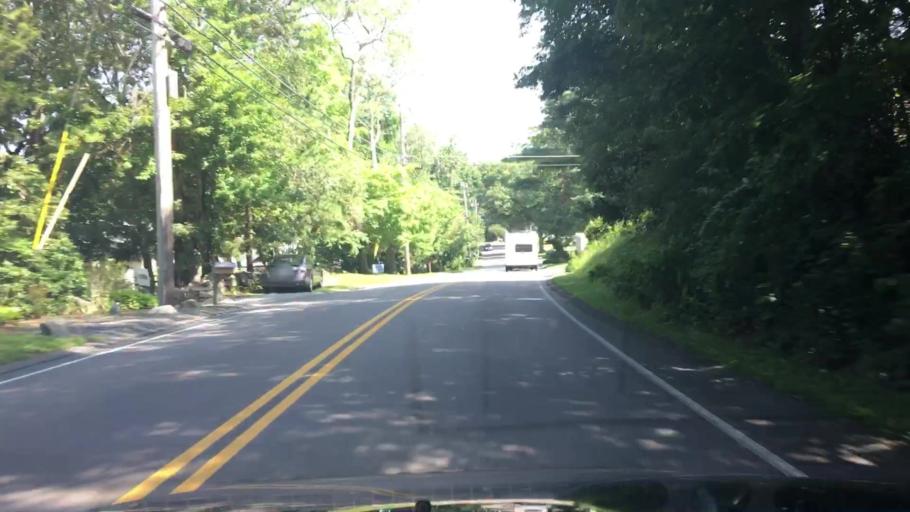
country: US
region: Massachusetts
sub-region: Middlesex County
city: Holliston
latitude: 42.1999
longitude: -71.4107
